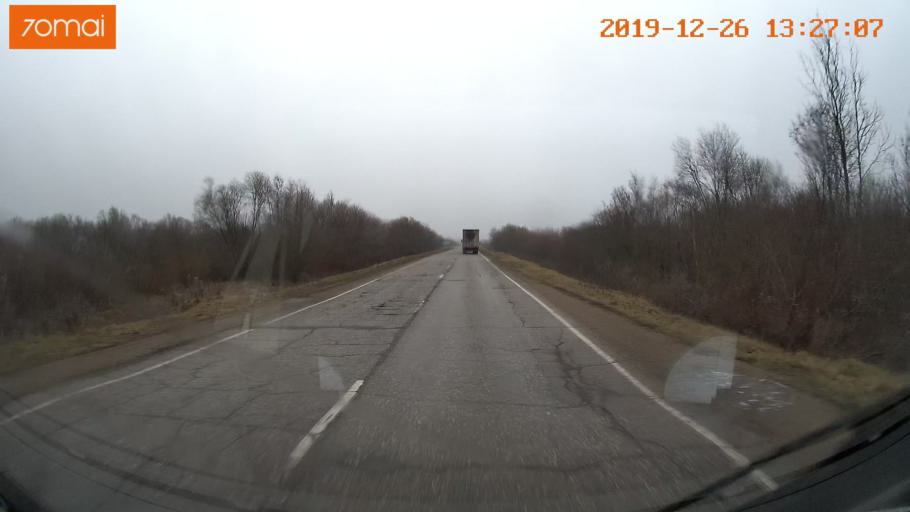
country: RU
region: Vologda
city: Cherepovets
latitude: 58.8560
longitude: 38.2368
